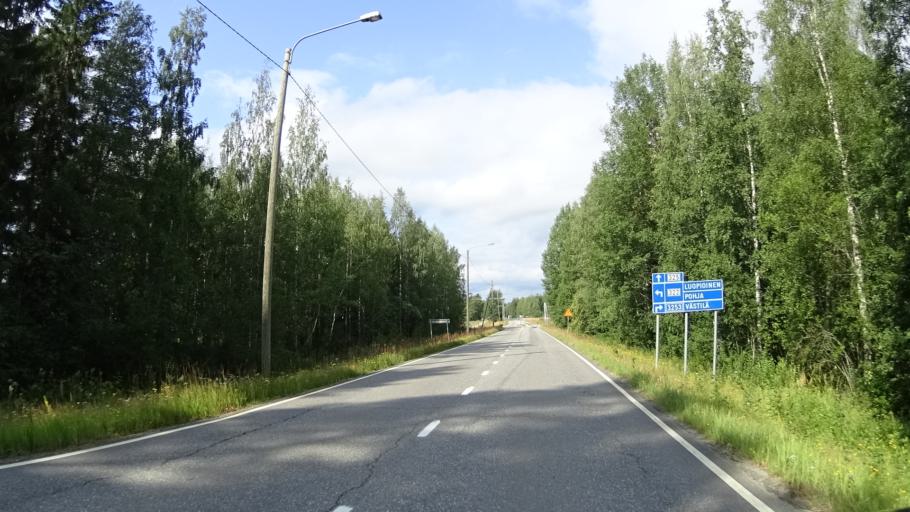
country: FI
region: Pirkanmaa
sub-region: Tampere
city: Luopioinen
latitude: 61.4827
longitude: 24.7137
